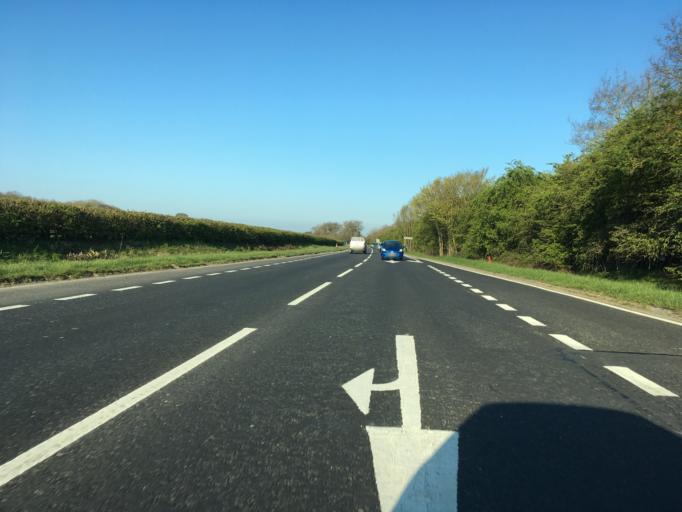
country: GB
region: England
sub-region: Oxfordshire
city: North Leigh
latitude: 51.7911
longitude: -1.4213
